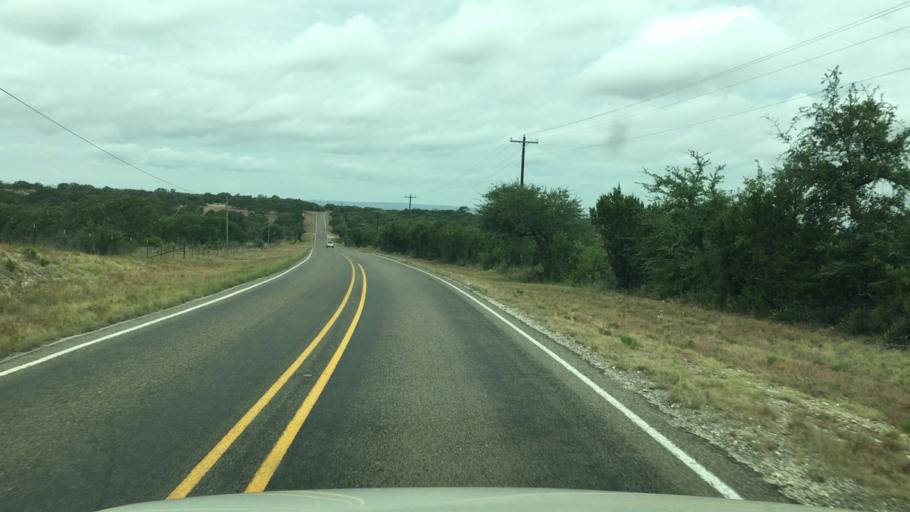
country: US
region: Texas
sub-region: Llano County
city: Horseshoe Bay
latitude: 30.4610
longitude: -98.4023
